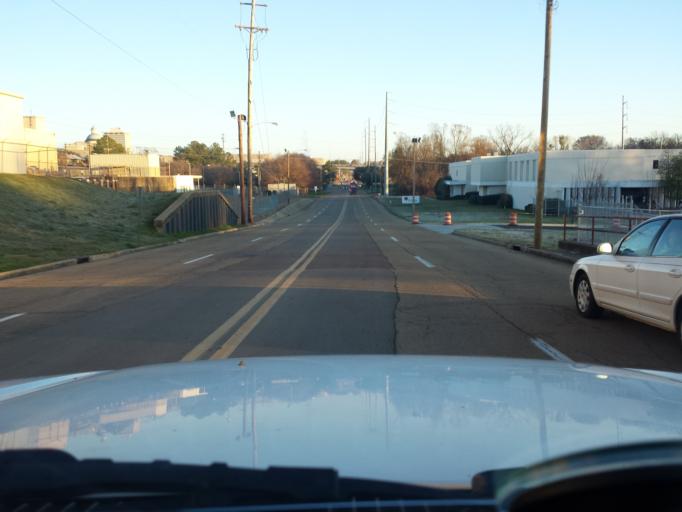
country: US
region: Mississippi
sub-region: Hinds County
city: Jackson
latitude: 32.2942
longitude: -90.1786
